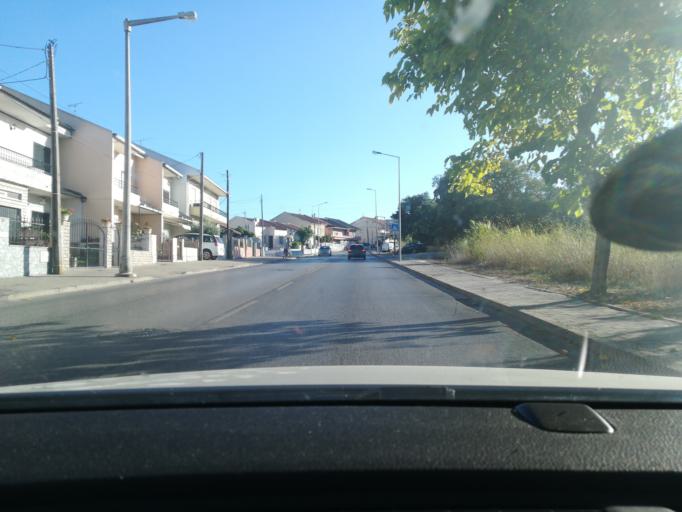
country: PT
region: Setubal
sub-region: Seixal
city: Corroios
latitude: 38.6332
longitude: -9.1584
